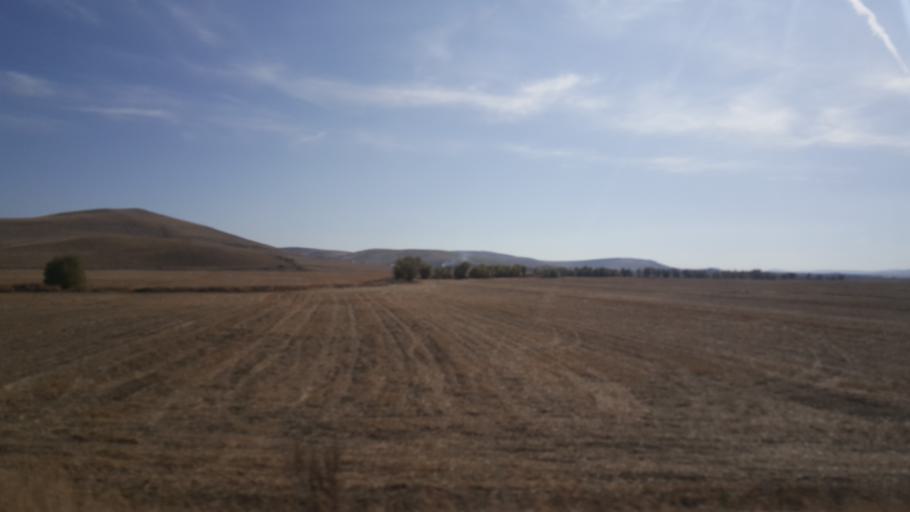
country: TR
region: Ankara
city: Yenice
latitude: 39.3828
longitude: 32.8142
